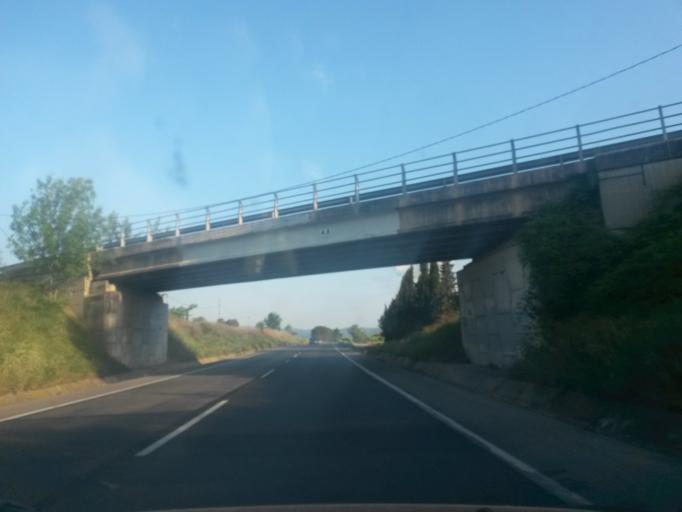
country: ES
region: Catalonia
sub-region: Provincia de Girona
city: Fontcoberta
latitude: 42.1175
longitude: 2.7884
